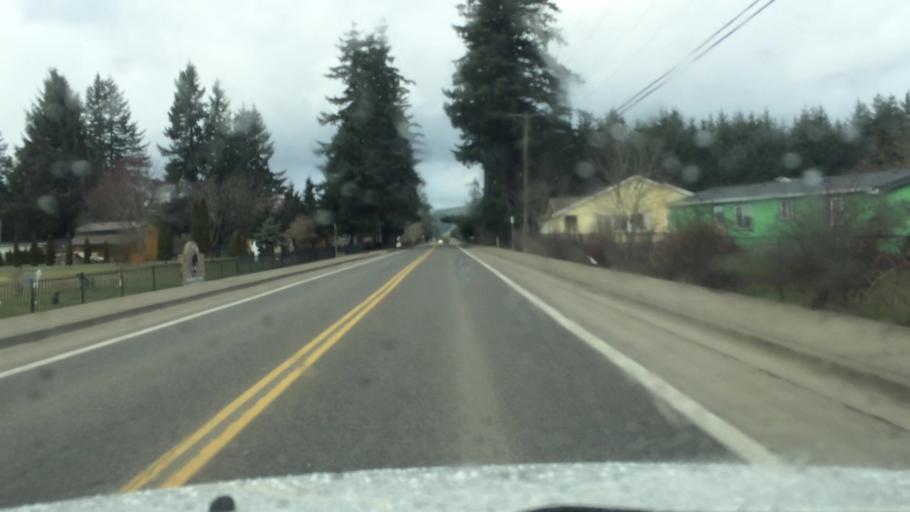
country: US
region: Oregon
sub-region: Polk County
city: Grand Ronde
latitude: 45.0683
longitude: -123.6119
